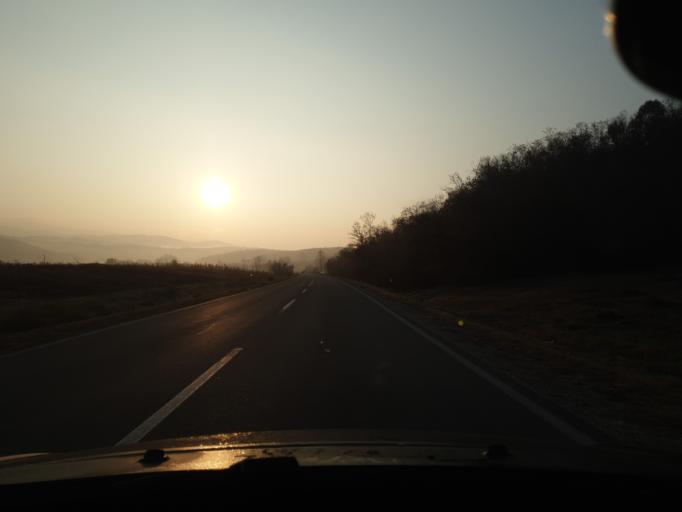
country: RS
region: Central Serbia
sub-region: Jablanicki Okrug
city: Leskovac
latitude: 42.9201
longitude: 22.0241
